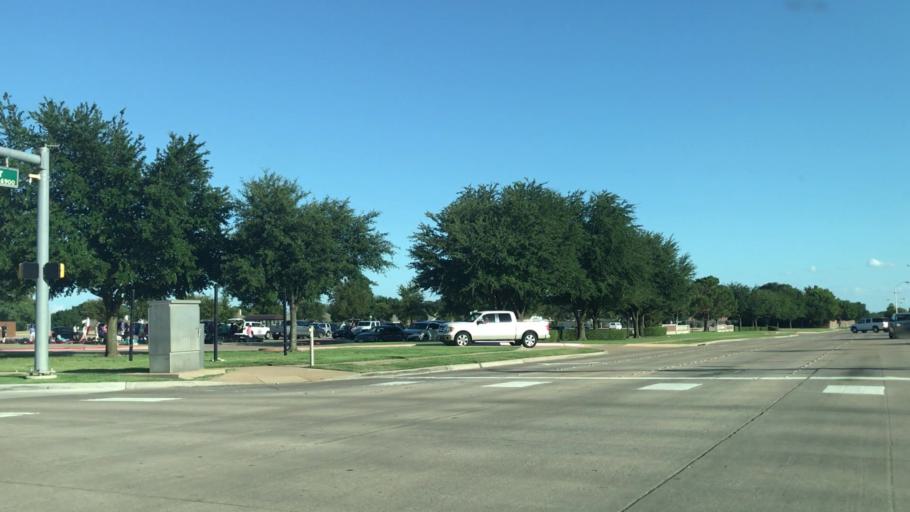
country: US
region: Texas
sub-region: Collin County
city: Plano
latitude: 33.0716
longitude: -96.7368
